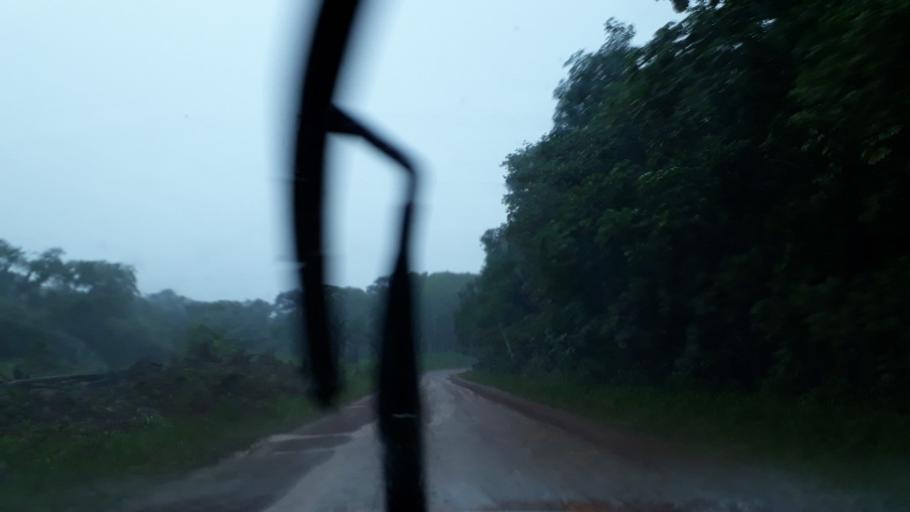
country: CD
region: Eastern Province
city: Kisangani
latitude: 0.4654
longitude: 25.5478
